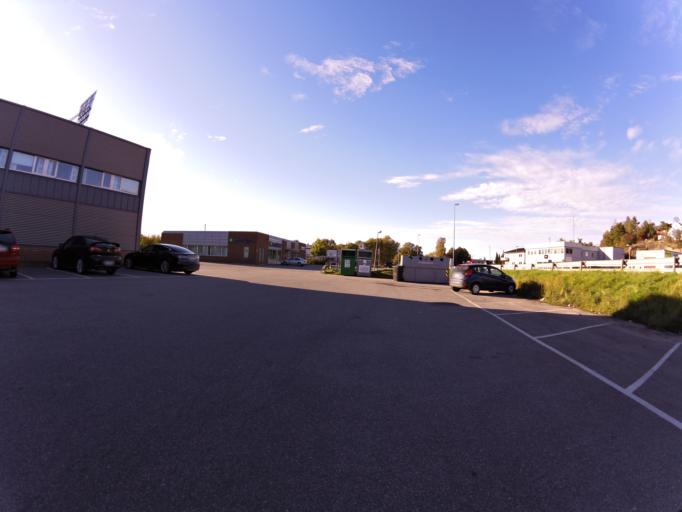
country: NO
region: Ostfold
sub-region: Sarpsborg
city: Sarpsborg
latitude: 59.2680
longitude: 11.0323
